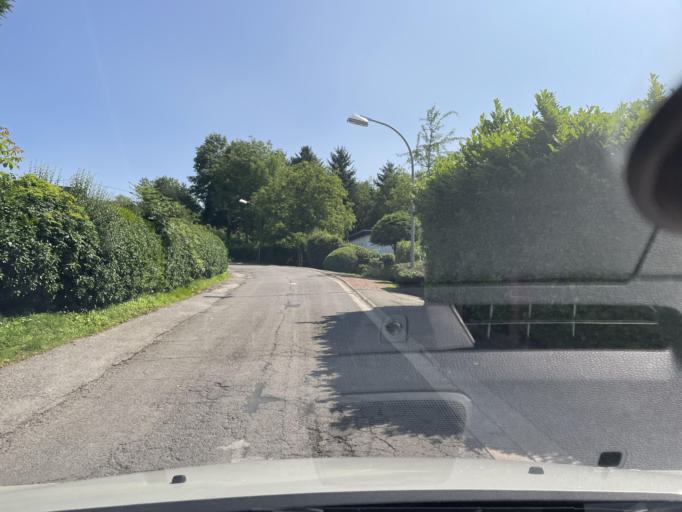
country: DE
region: Saarland
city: Sulzbach
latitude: 49.2304
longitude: 7.0575
